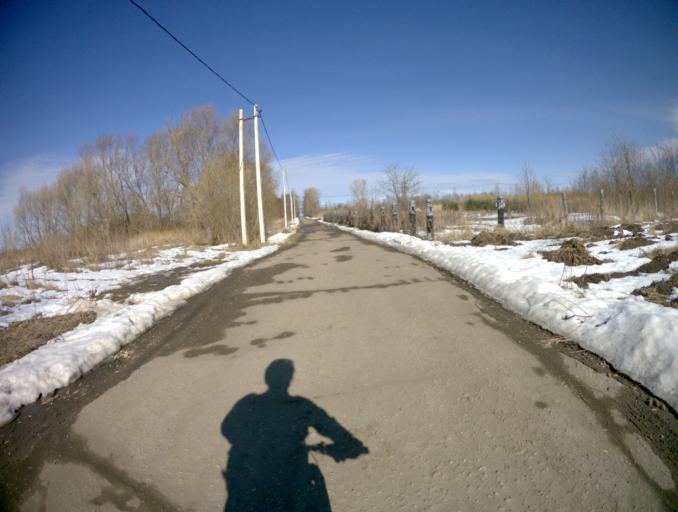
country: RU
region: Vladimir
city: Suzdal'
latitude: 56.4274
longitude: 40.4579
